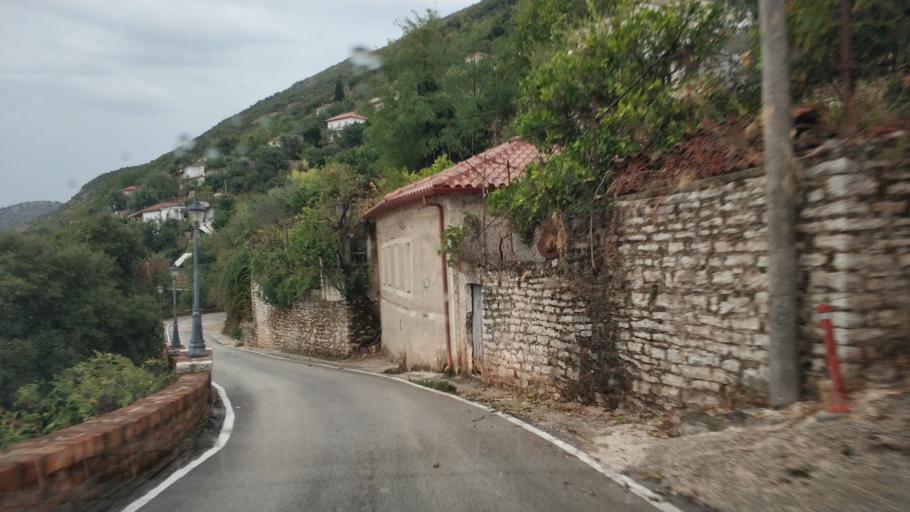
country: AL
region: Vlore
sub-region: Rrethi i Sarandes
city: Lukove
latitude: 39.9472
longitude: 19.9682
